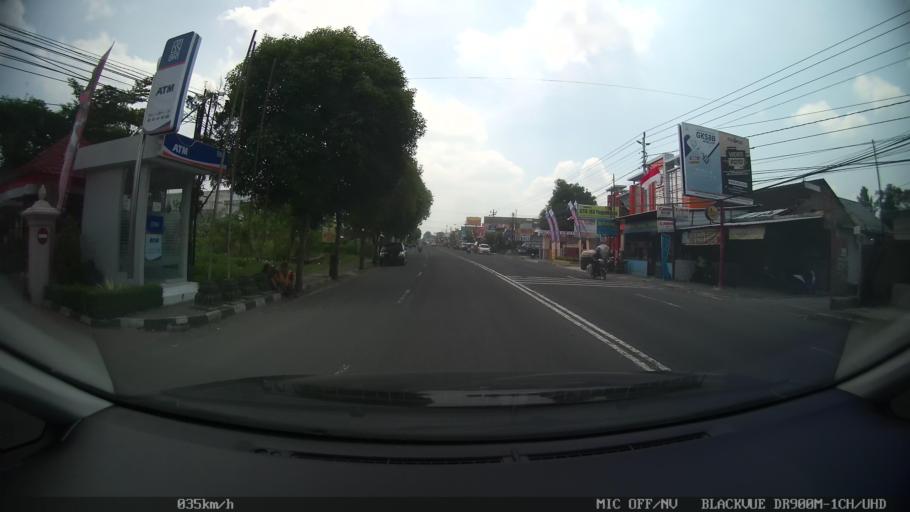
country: ID
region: Daerah Istimewa Yogyakarta
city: Yogyakarta
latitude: -7.8174
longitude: 110.4019
